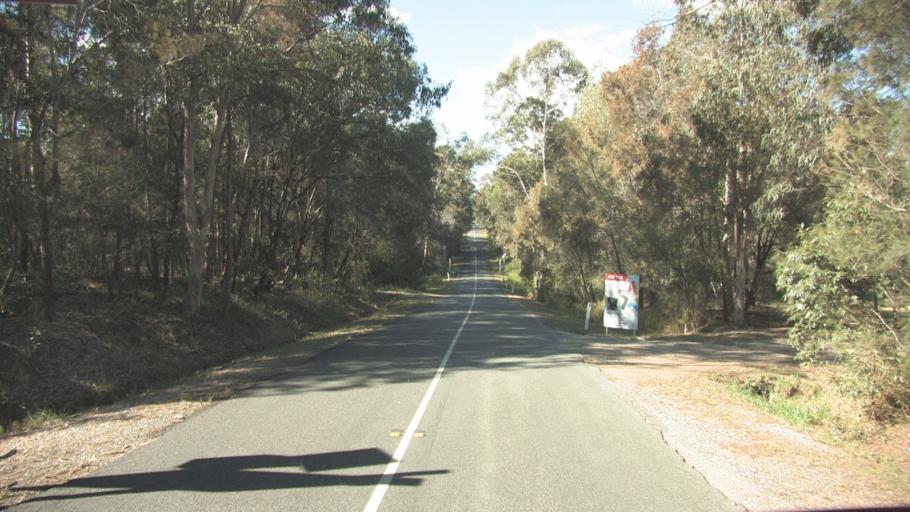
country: AU
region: Queensland
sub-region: Logan
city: Chambers Flat
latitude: -27.7910
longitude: 153.0878
